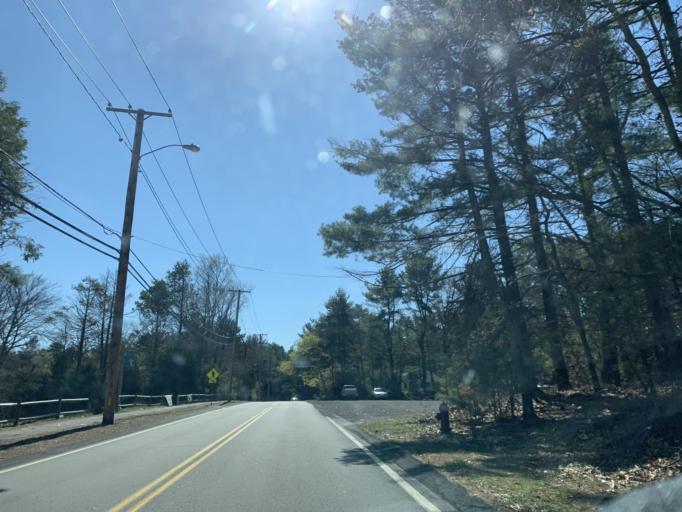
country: US
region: Massachusetts
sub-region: Norfolk County
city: Walpole
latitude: 42.1536
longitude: -71.2172
